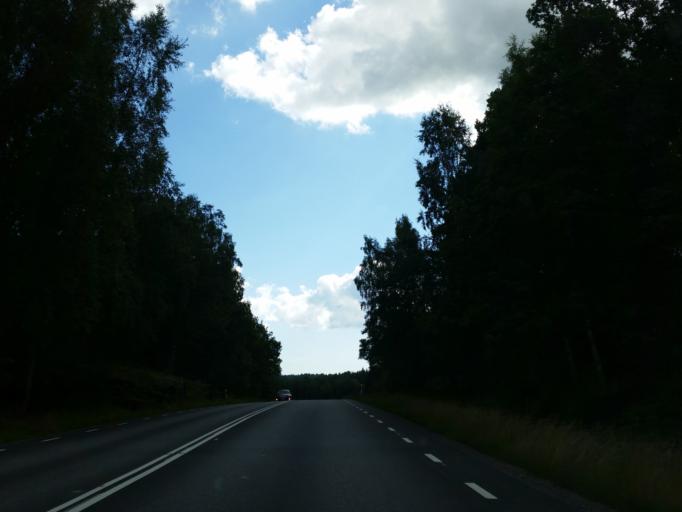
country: SE
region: Soedermanland
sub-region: Trosa Kommun
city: Vagnharad
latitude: 58.9606
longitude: 17.5606
